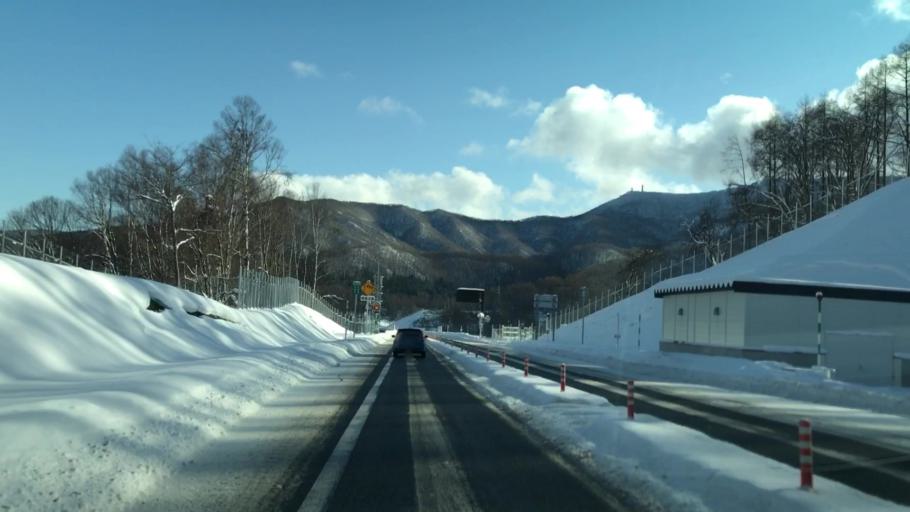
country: JP
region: Hokkaido
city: Otaru
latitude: 43.1681
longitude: 140.9831
